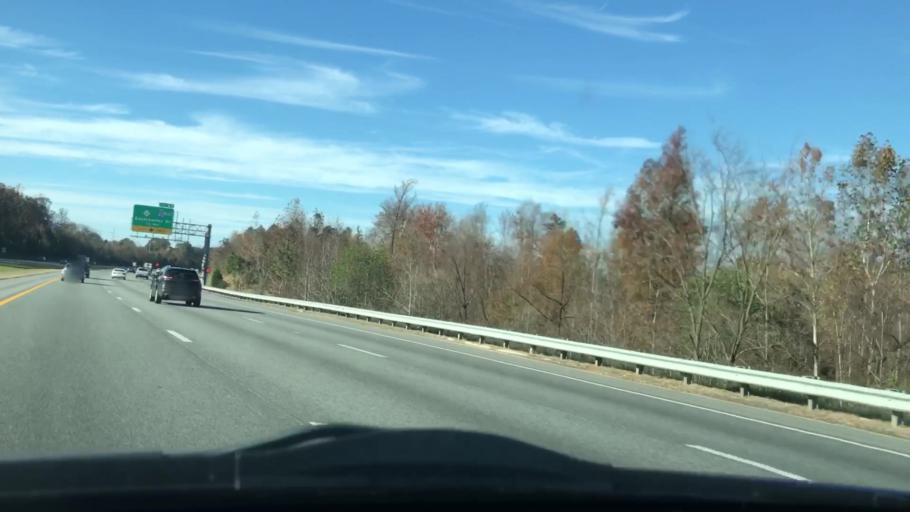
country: US
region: North Carolina
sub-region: Guilford County
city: High Point
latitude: 35.9909
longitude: -79.9824
